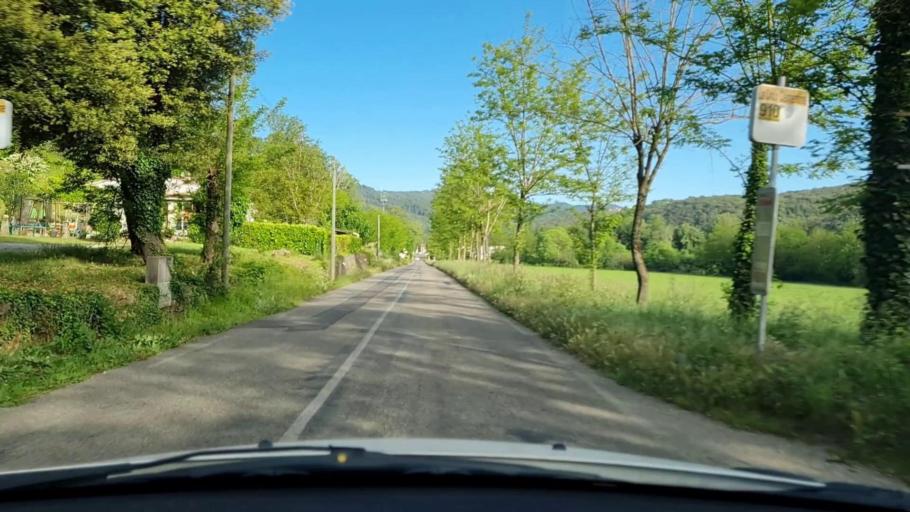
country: FR
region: Languedoc-Roussillon
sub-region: Departement du Gard
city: Cendras
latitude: 44.1521
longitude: 4.0430
